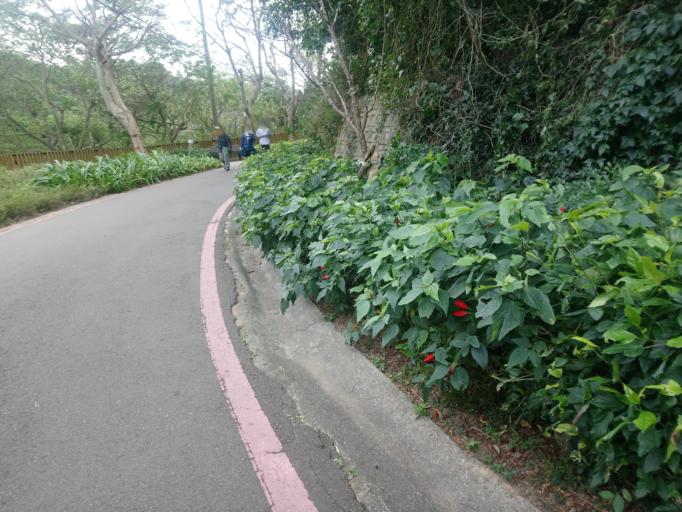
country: TW
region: Taiwan
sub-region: Hsinchu
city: Hsinchu
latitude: 24.7940
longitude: 120.9868
